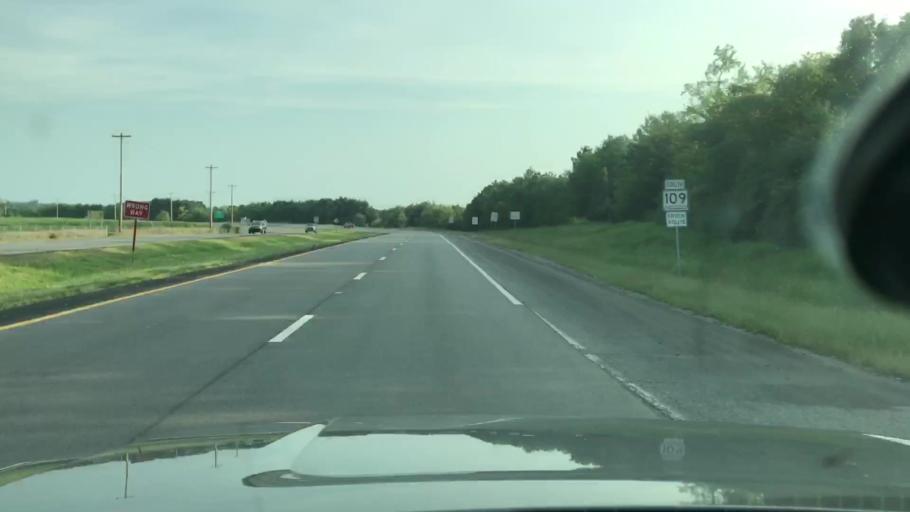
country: US
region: Tennessee
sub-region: Sumner County
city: Gallatin
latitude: 36.3911
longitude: -86.4728
